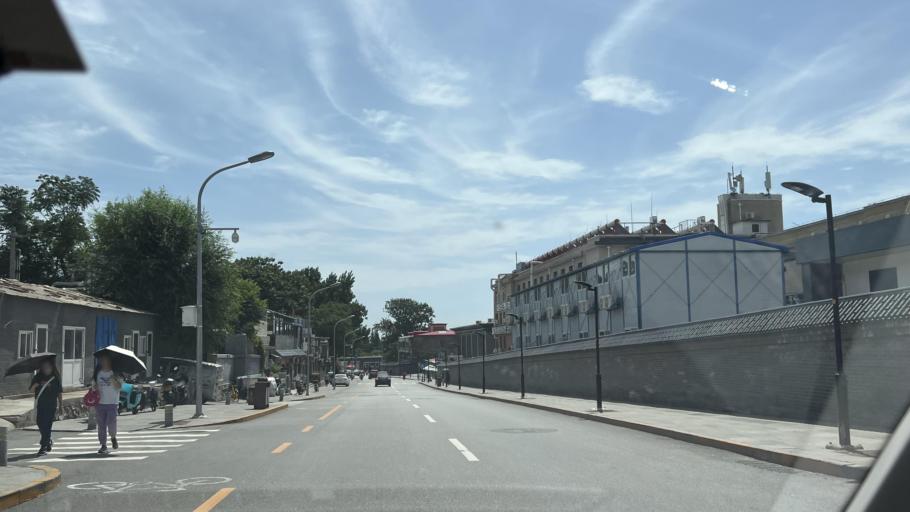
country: CN
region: Beijing
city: Xiangshan
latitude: 39.9918
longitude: 116.2013
